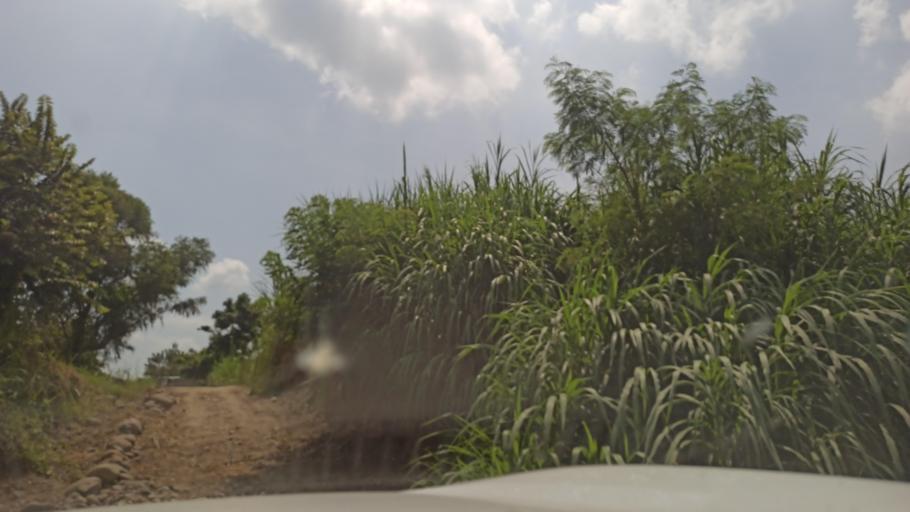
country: MX
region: Veracruz
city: Martinez de la Torre
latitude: 20.0793
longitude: -97.0764
